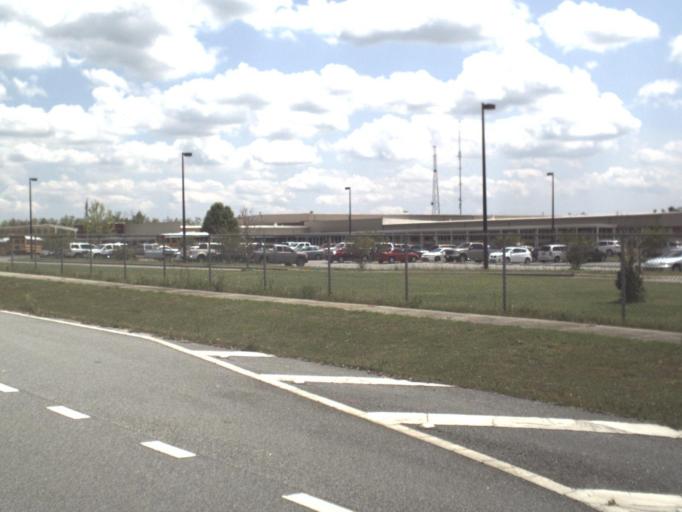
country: US
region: Florida
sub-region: Escambia County
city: Molino
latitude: 30.7423
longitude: -87.3629
